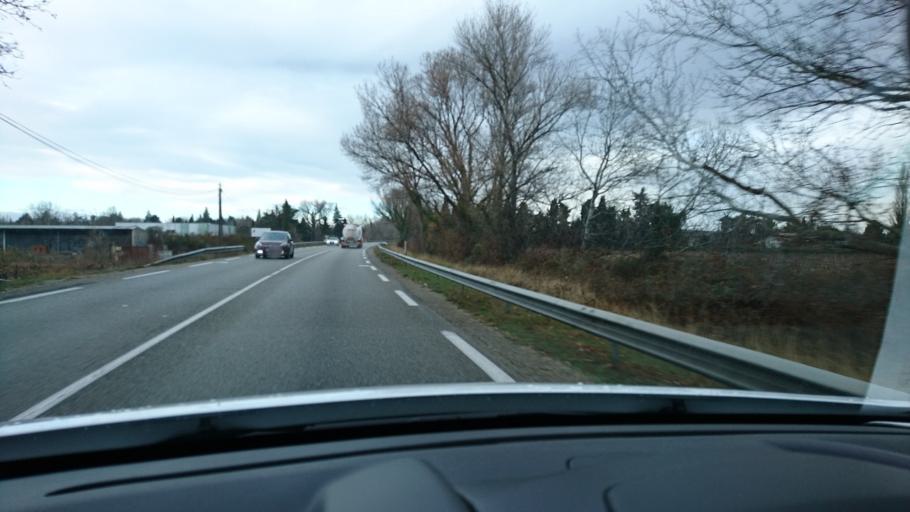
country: FR
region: Languedoc-Roussillon
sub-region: Departement du Gard
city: Pujaut
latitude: 43.9959
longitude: 4.7394
